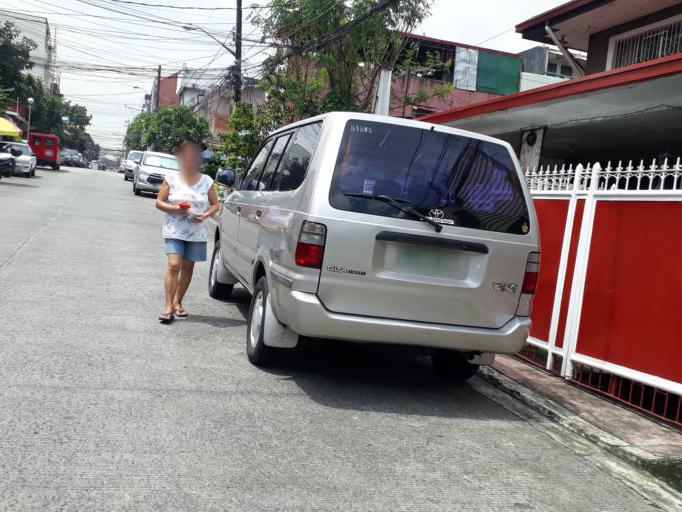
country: PH
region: Calabarzon
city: Bagong Pagasa
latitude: 14.6640
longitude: 121.0323
